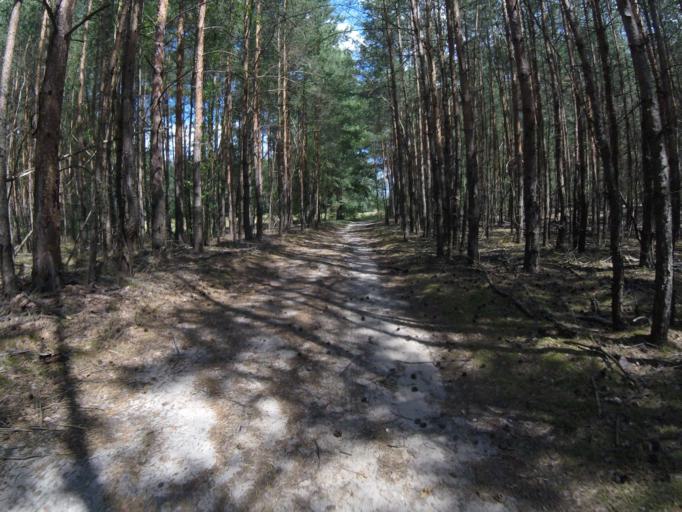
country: DE
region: Brandenburg
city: Bestensee
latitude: 52.2149
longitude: 13.6425
